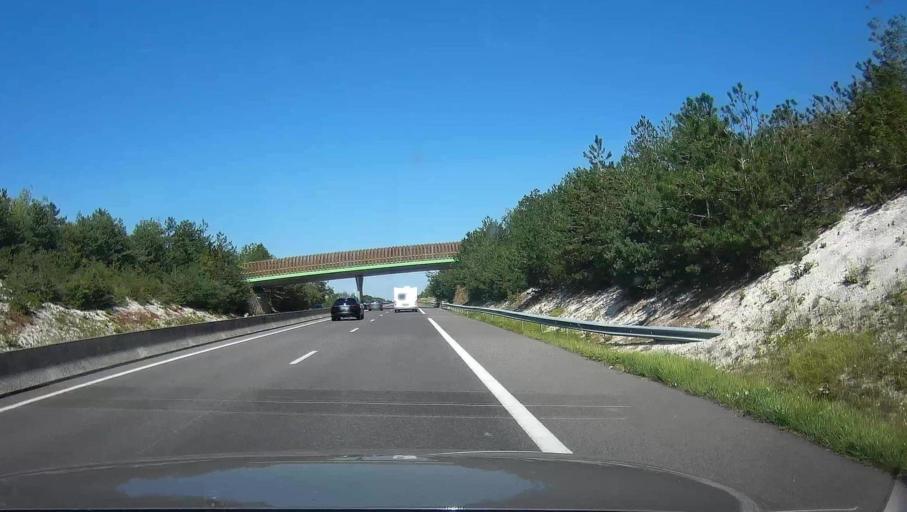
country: FR
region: Champagne-Ardenne
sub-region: Departement de l'Aube
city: Arcis-sur-Aube
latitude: 48.5763
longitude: 4.1892
